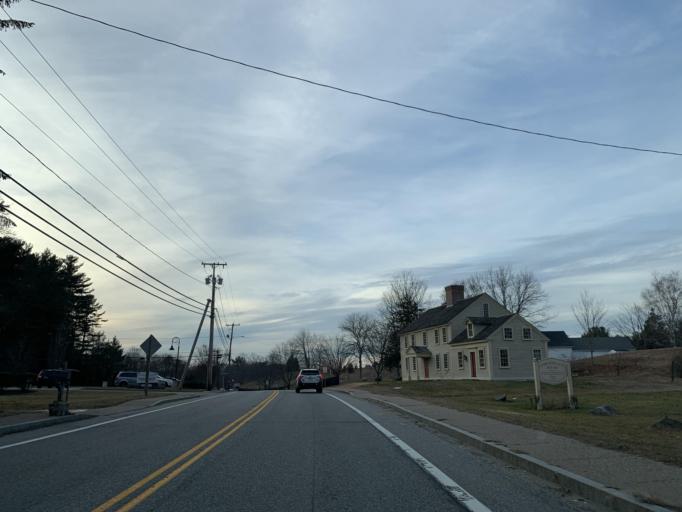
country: US
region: Rhode Island
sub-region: Providence County
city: Chepachet
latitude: 41.9074
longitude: -71.6633
